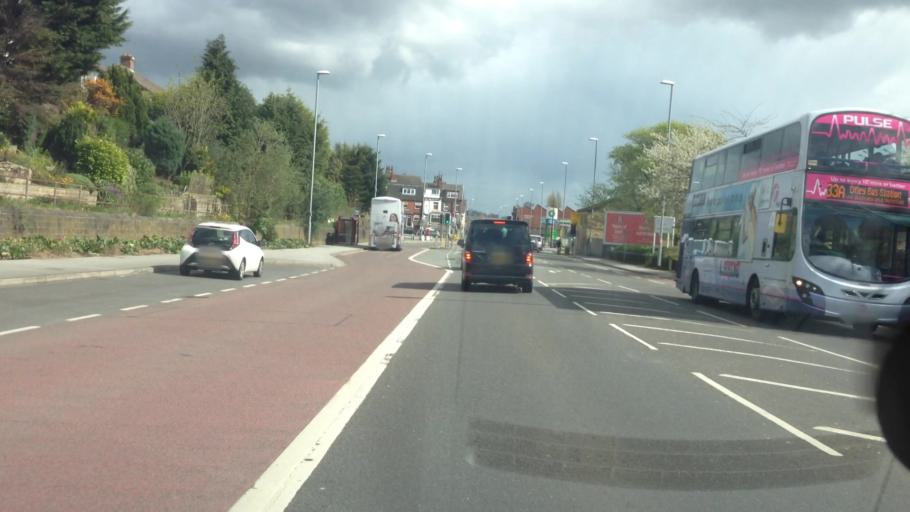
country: GB
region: England
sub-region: City and Borough of Leeds
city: Leeds
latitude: 53.8097
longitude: -1.5919
